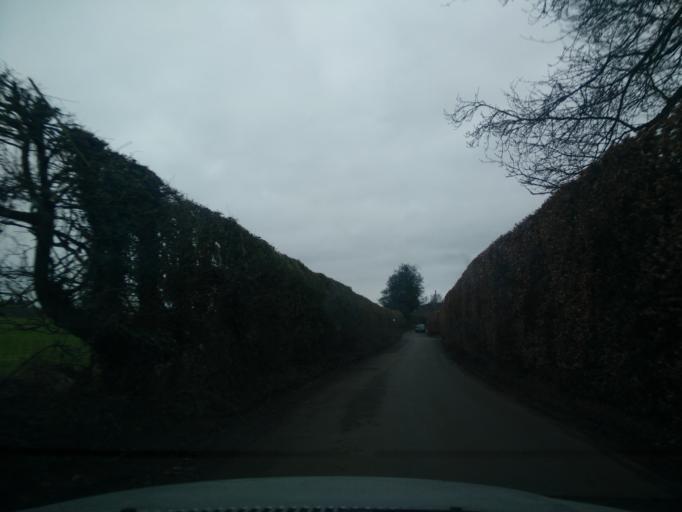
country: GB
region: England
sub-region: Buckinghamshire
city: Little Chalfont
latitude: 51.6523
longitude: -0.5494
